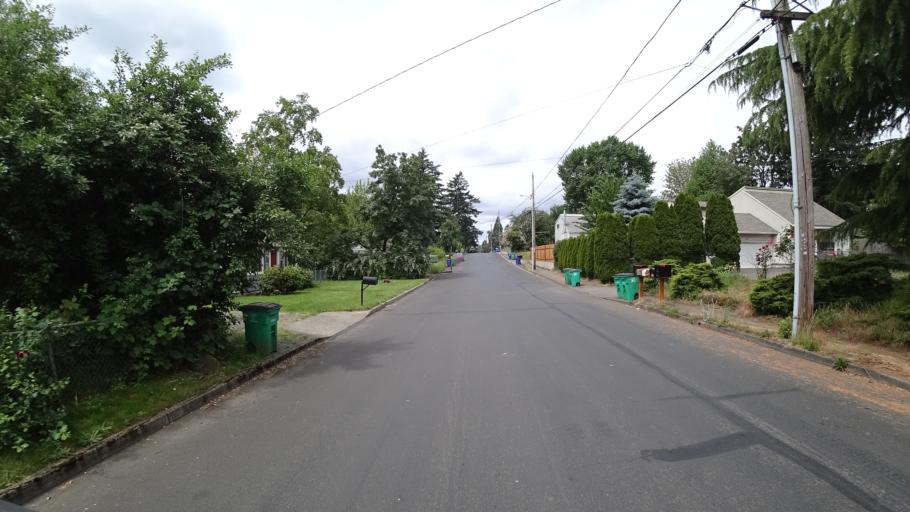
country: US
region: Oregon
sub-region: Multnomah County
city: Lents
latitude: 45.4702
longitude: -122.5705
